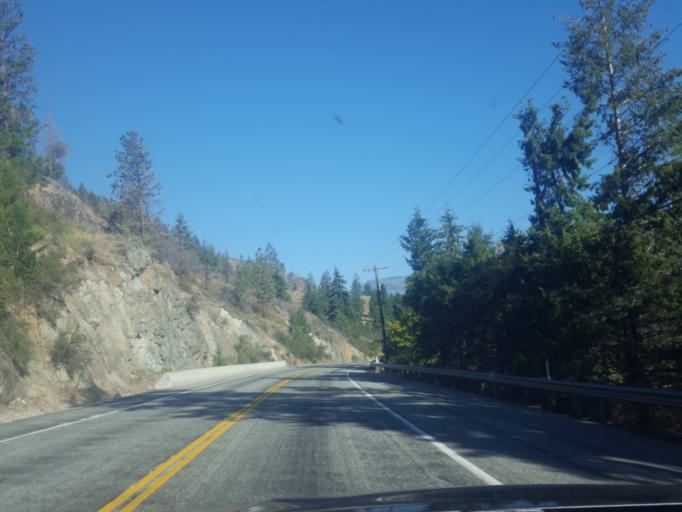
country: US
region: Washington
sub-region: Chelan County
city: Granite Falls
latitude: 47.9818
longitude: -120.2285
